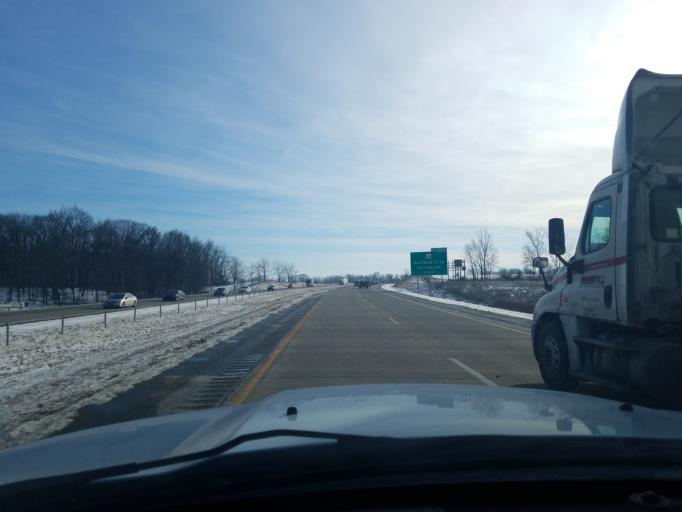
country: US
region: Indiana
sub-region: Grant County
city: Upland
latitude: 40.4428
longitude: -85.5445
